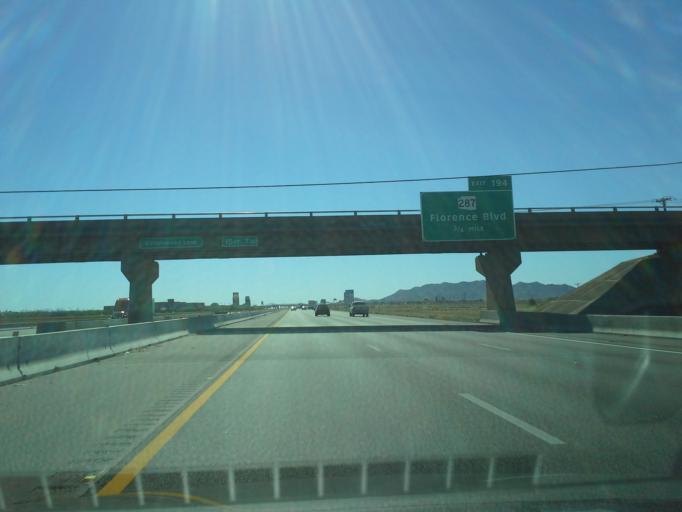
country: US
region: Arizona
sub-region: Pinal County
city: Casa Grande
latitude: 32.8948
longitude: -111.6870
